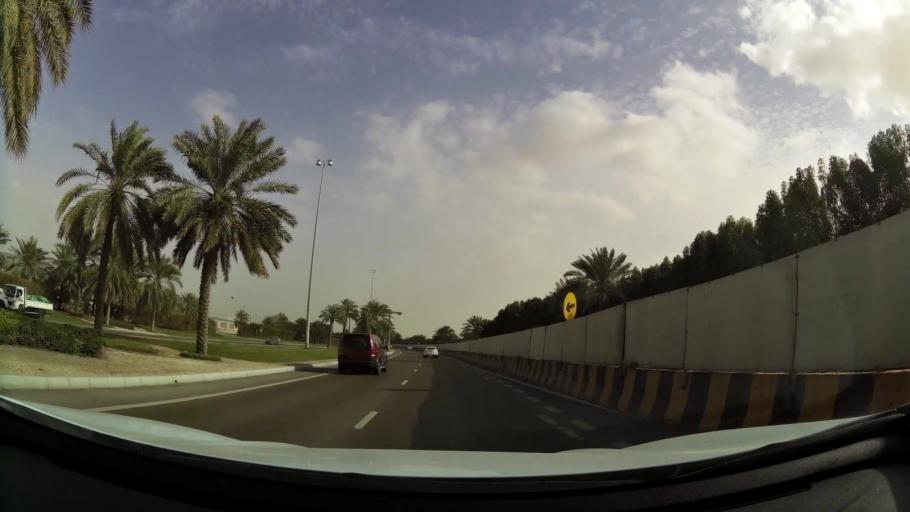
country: AE
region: Abu Dhabi
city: Abu Dhabi
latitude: 24.4374
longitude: 54.6233
